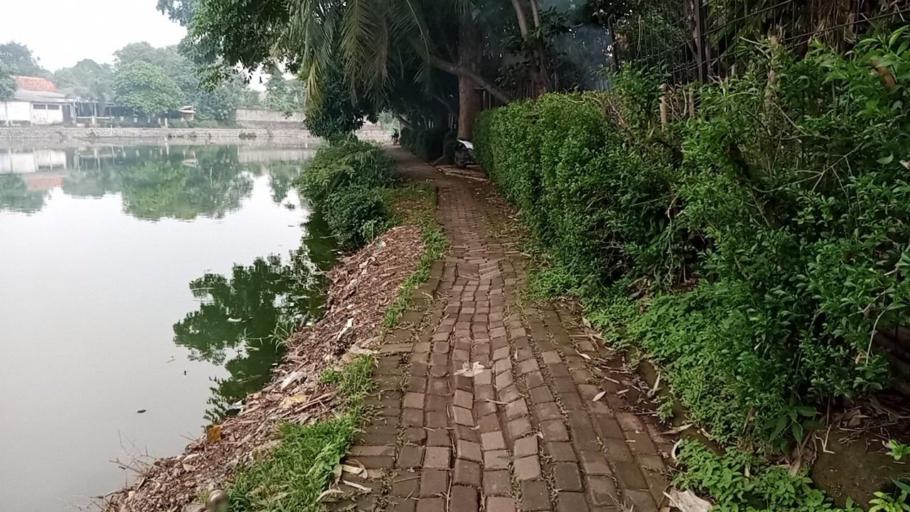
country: ID
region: West Java
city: Depok
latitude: -6.4466
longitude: 106.8005
